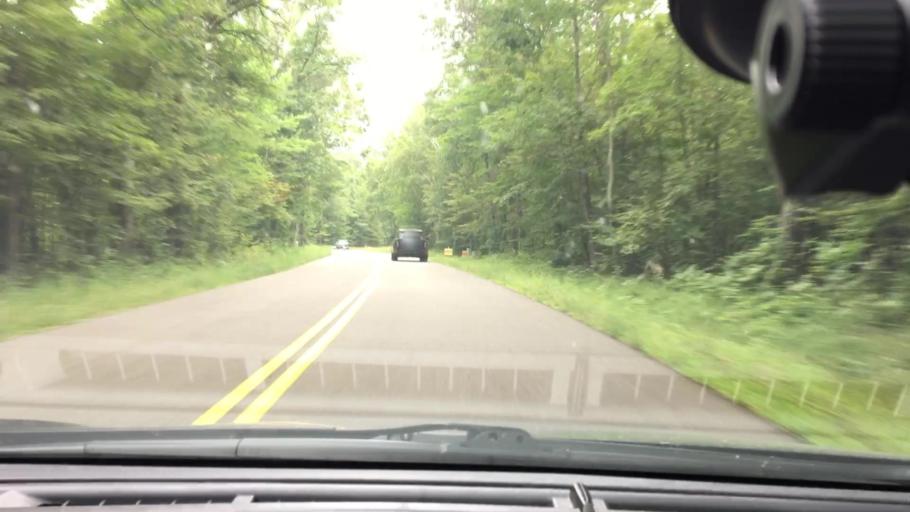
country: US
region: Minnesota
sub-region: Crow Wing County
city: Cross Lake
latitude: 46.6702
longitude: -94.0400
